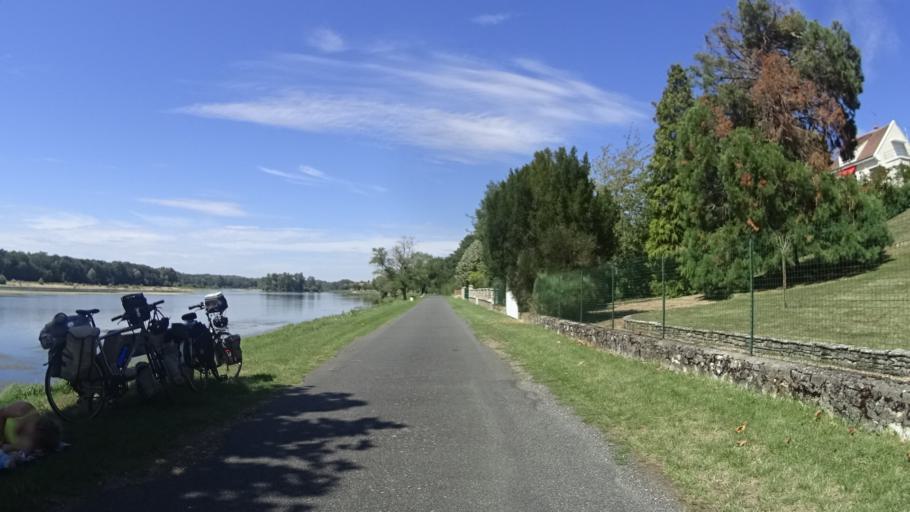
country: FR
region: Centre
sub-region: Departement du Loiret
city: Bonny-sur-Loire
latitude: 47.5853
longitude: 2.7956
